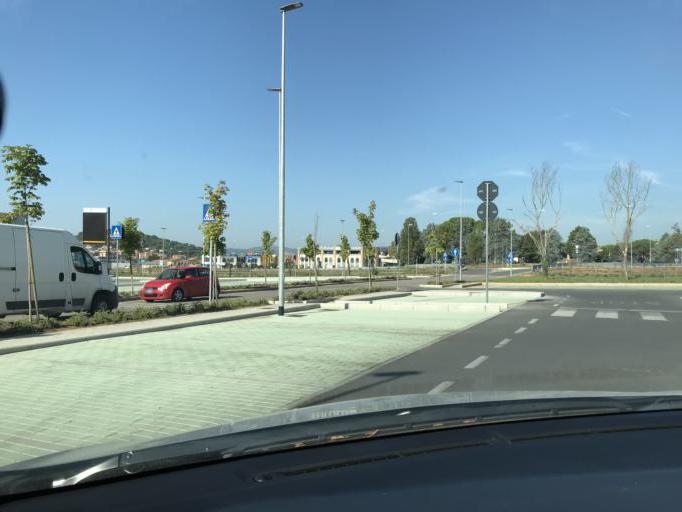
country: IT
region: Umbria
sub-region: Provincia di Perugia
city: Lacugnano
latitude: 43.1005
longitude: 12.3225
